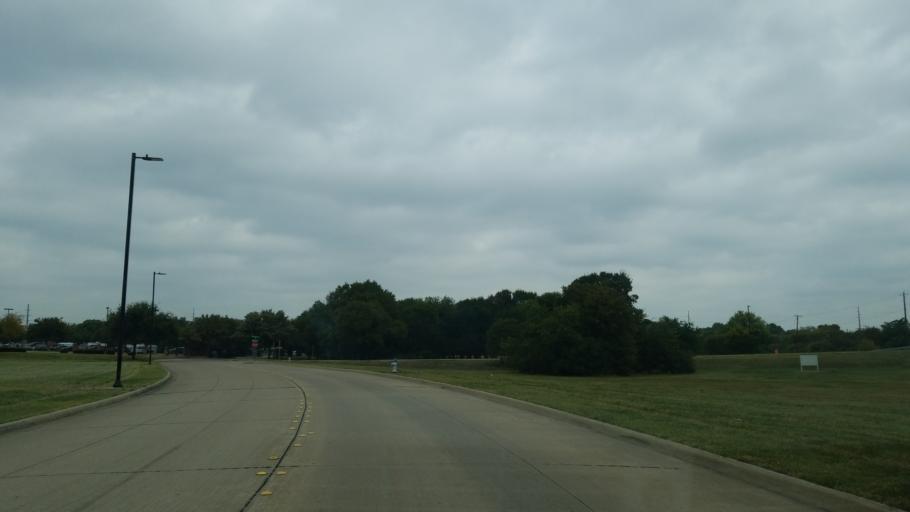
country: US
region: Texas
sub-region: Dallas County
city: Garland
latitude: 32.9097
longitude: -96.6530
